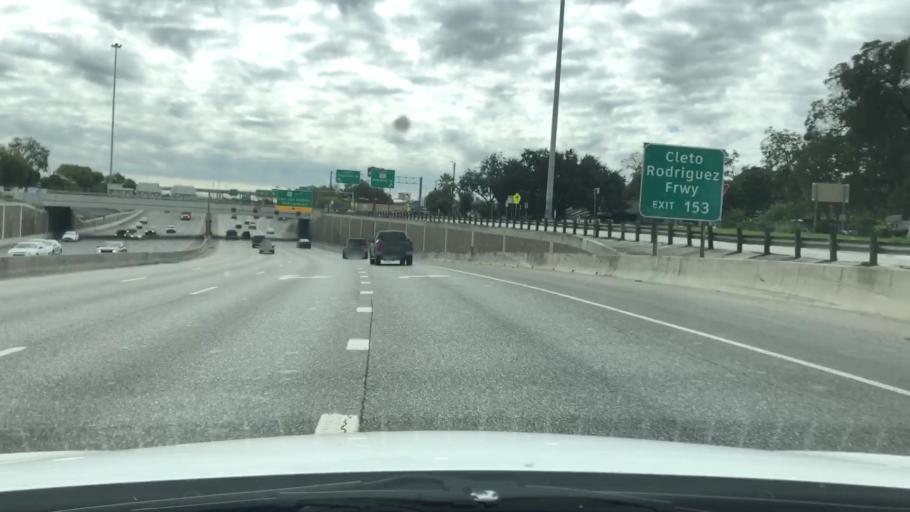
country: US
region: Texas
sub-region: Bexar County
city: San Antonio
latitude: 29.4021
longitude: -98.5121
